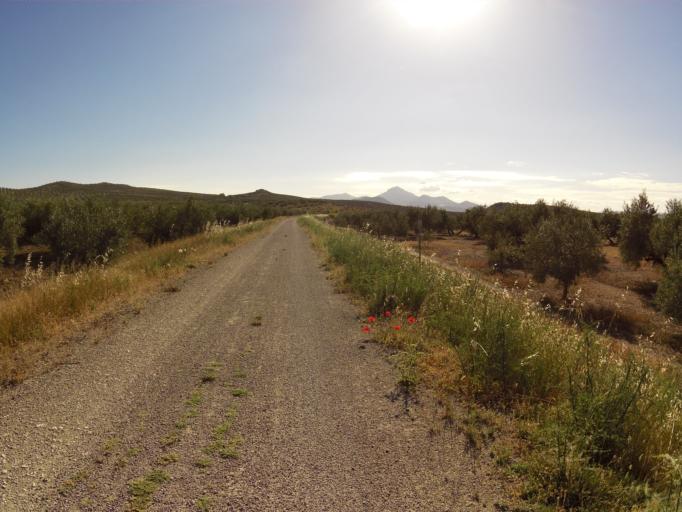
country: ES
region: Andalusia
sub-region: Province of Cordoba
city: Luque
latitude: 37.5823
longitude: -4.2111
